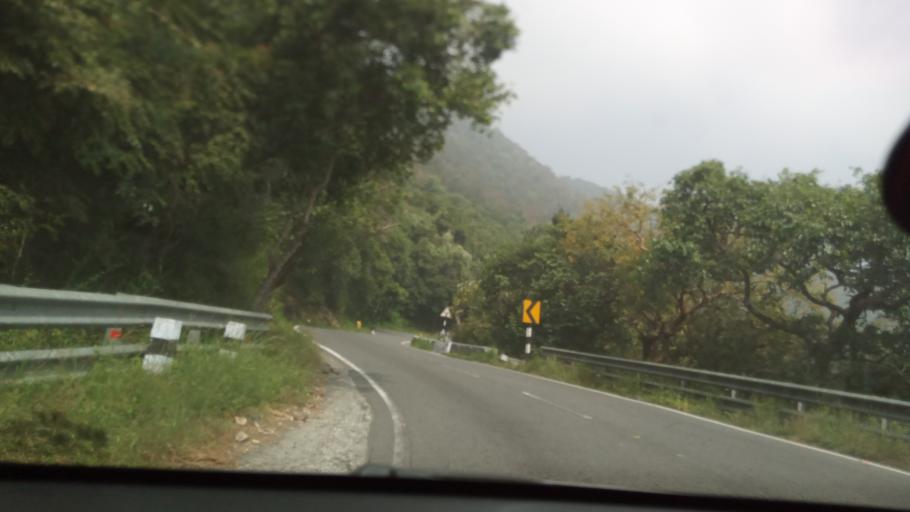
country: IN
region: Tamil Nadu
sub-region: Erode
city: Sathyamangalam
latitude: 11.5975
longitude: 77.1250
